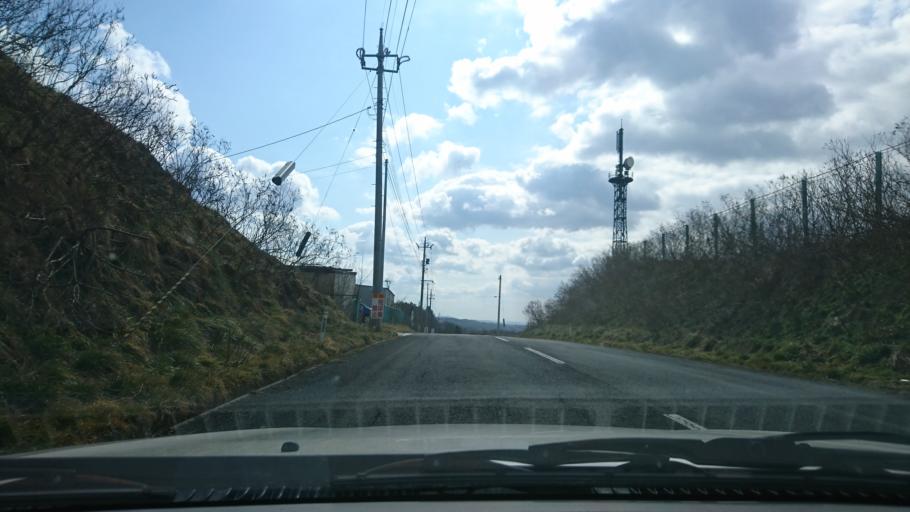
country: JP
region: Iwate
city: Ichinoseki
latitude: 38.8107
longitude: 141.2604
